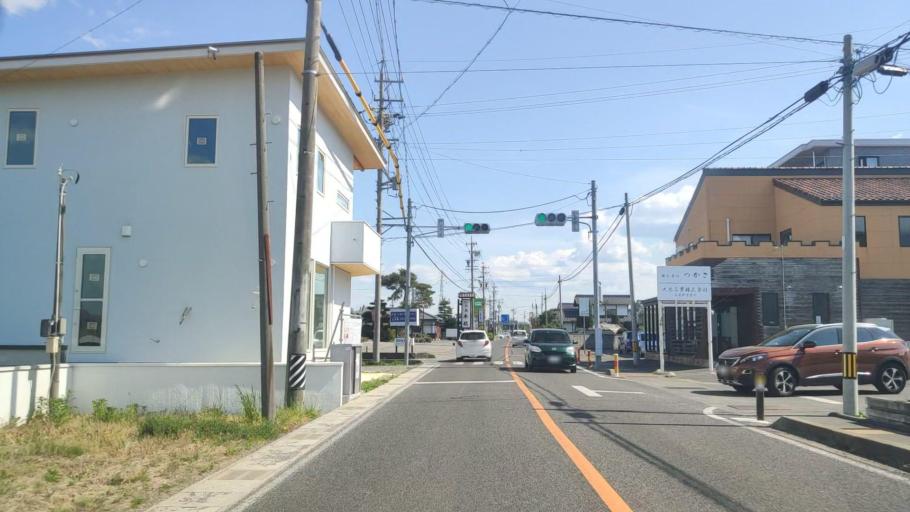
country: JP
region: Nagano
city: Toyoshina
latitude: 36.2883
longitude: 137.9076
